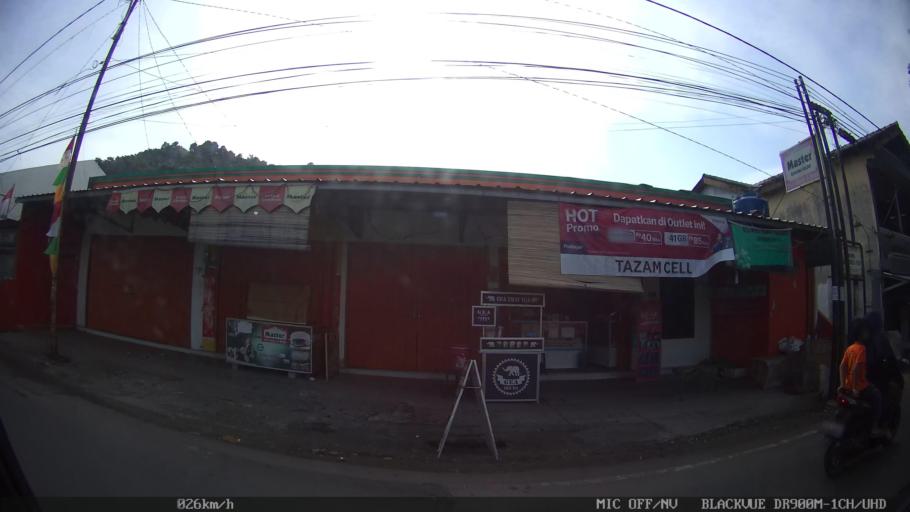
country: ID
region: Lampung
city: Kedaton
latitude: -5.3903
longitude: 105.2665
